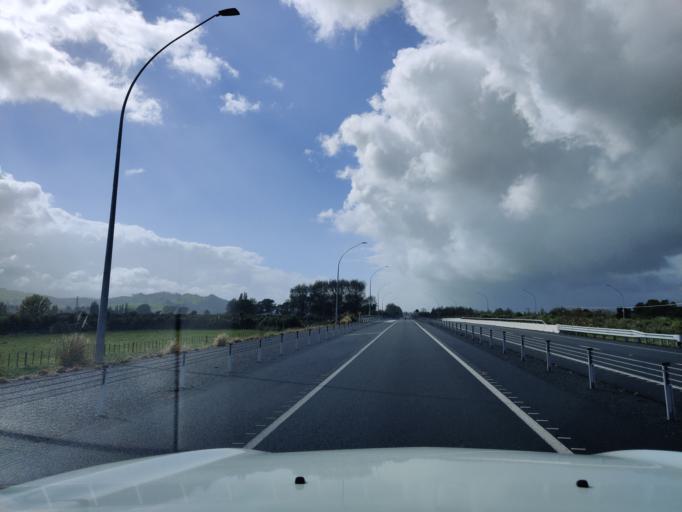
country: NZ
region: Waikato
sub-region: Waipa District
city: Cambridge
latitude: -37.8943
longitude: 175.5037
